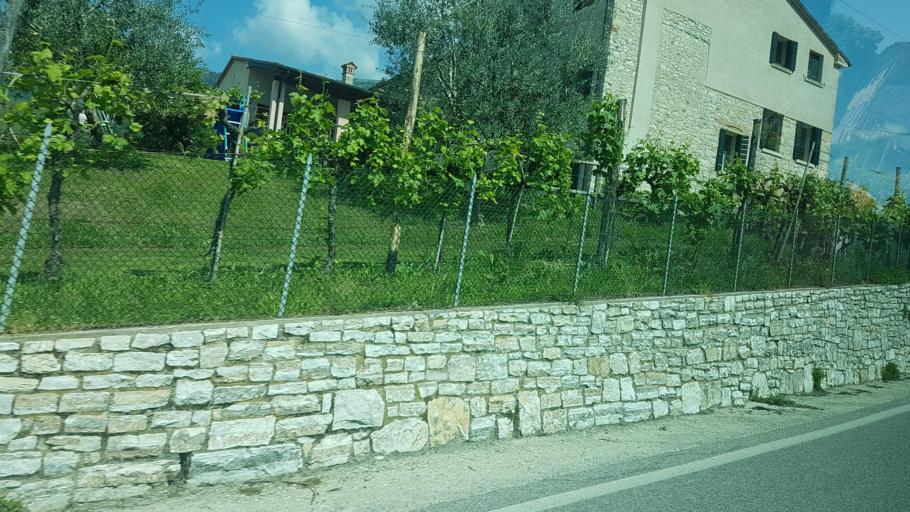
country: IT
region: Veneto
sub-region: Provincia di Treviso
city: Vidor
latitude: 45.8948
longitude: 12.0398
